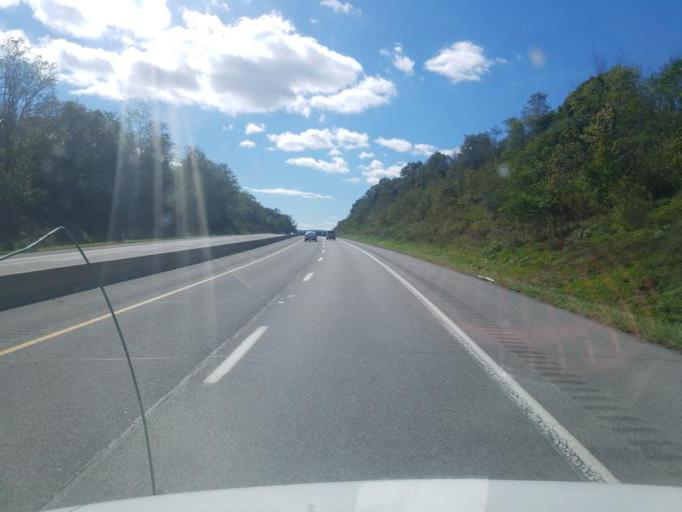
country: US
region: Pennsylvania
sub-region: Bedford County
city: Everett
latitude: 40.0241
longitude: -78.3781
